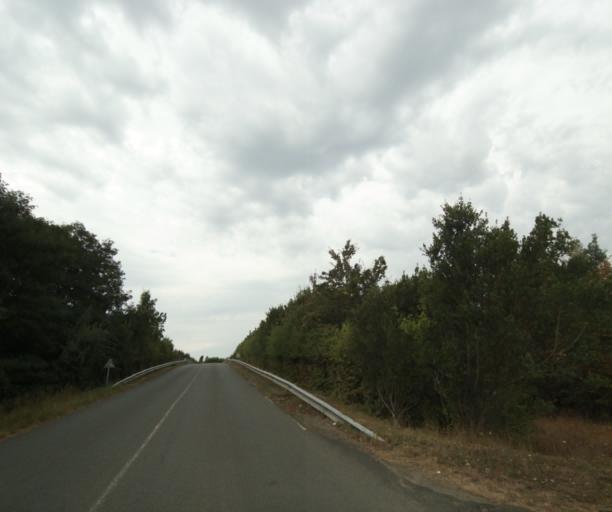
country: FR
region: Poitou-Charentes
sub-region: Departement de la Charente-Maritime
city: Tonnay-Charente
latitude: 45.9607
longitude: -0.8732
